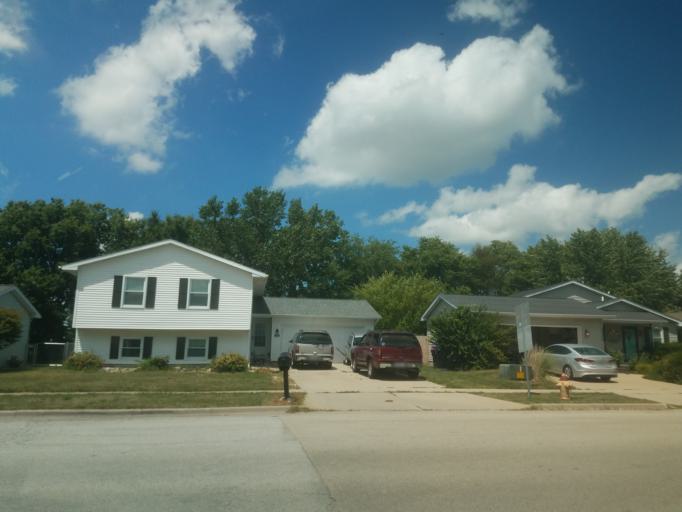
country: US
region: Illinois
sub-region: McLean County
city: Bloomington
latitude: 40.4469
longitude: -89.0305
